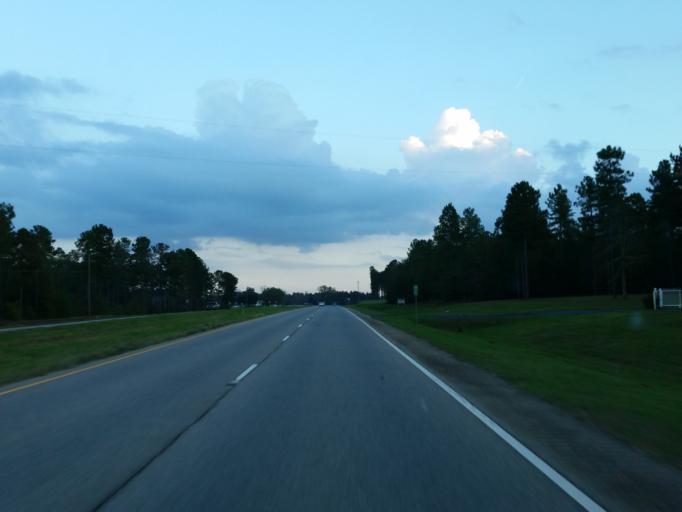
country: US
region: Georgia
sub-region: Pulaski County
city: Hawkinsville
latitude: 32.3415
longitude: -83.5699
